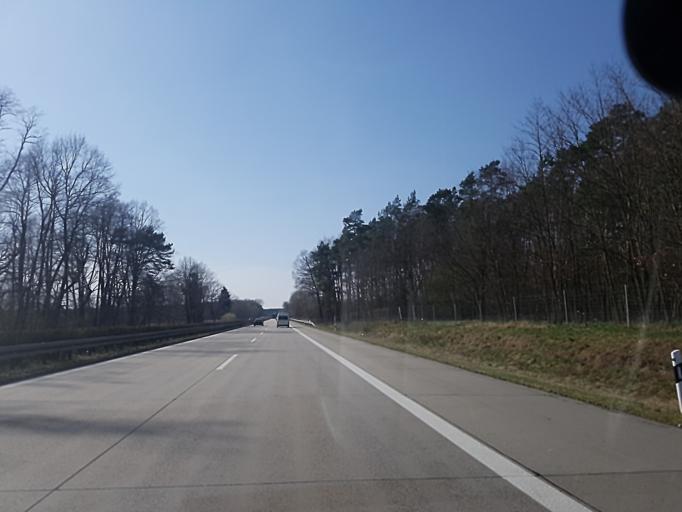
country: DE
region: Brandenburg
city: Heinersbruck
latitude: 51.7126
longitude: 14.4901
